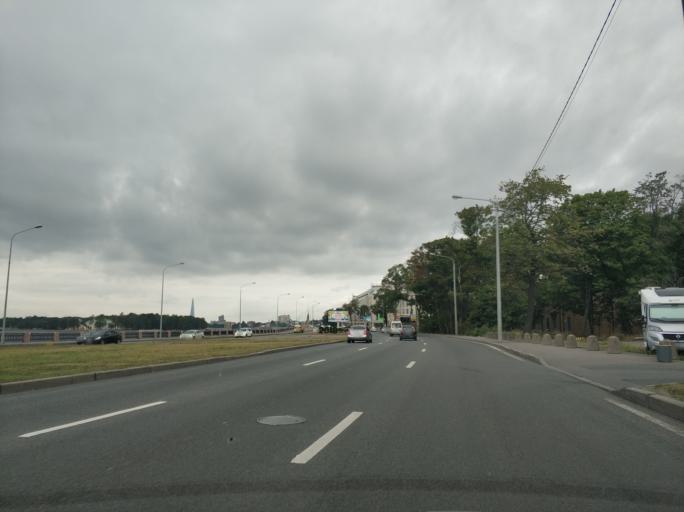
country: RU
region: St.-Petersburg
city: Petrogradka
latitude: 59.9802
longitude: 30.3219
